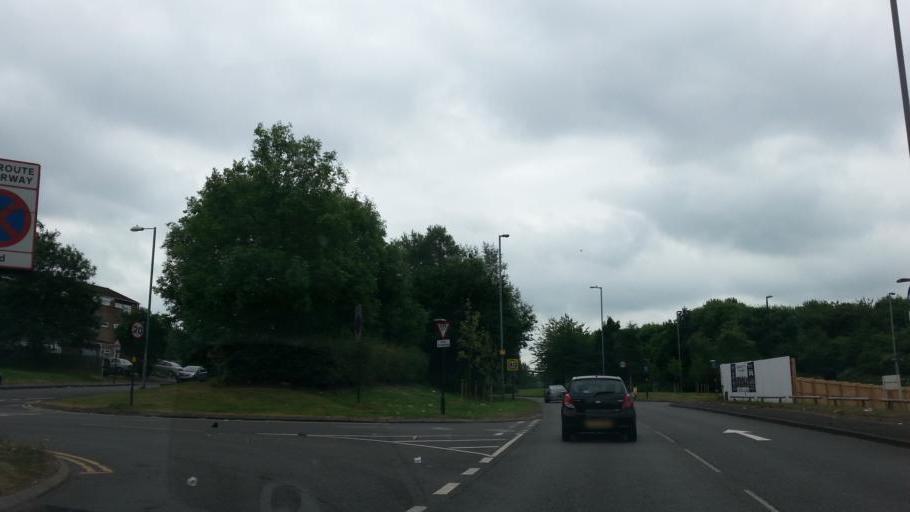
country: GB
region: England
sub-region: City and Borough of Birmingham
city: Birmingham
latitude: 52.4704
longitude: -1.8717
